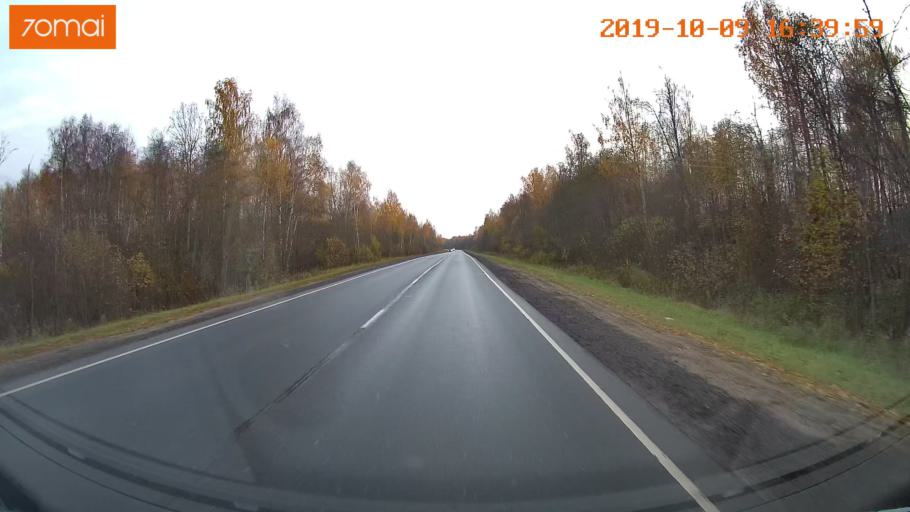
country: RU
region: Kostroma
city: Volgorechensk
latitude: 57.4902
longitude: 41.0550
